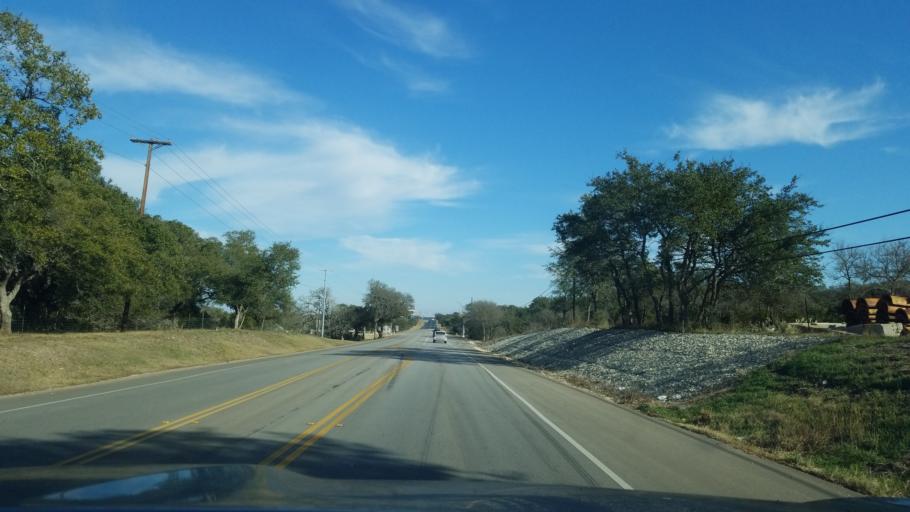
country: US
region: Texas
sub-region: Comal County
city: Canyon Lake
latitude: 29.7736
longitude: -98.2915
